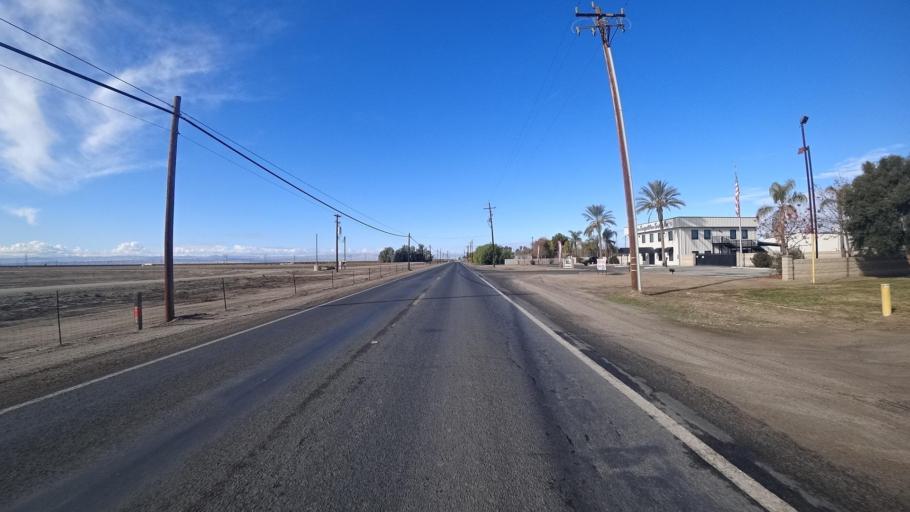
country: US
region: California
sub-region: Kern County
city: Rosedale
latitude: 35.3835
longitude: -119.2473
